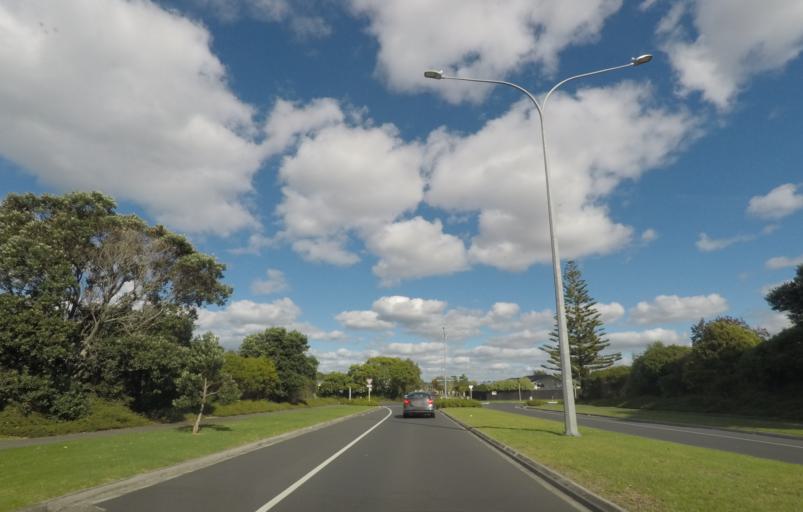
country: NZ
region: Auckland
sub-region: Auckland
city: Rothesay Bay
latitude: -36.5860
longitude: 174.6864
